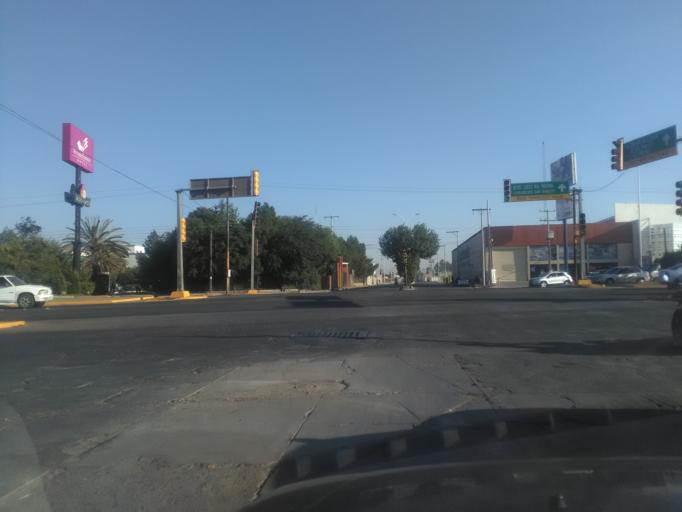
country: MX
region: Durango
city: Victoria de Durango
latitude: 24.0466
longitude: -104.6237
